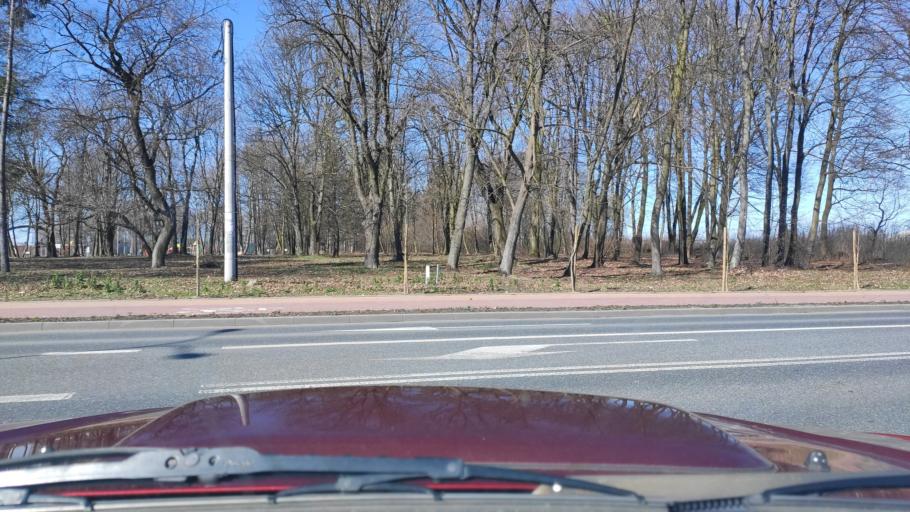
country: PL
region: Masovian Voivodeship
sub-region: Powiat zwolenski
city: Zwolen
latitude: 51.3611
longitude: 21.5829
